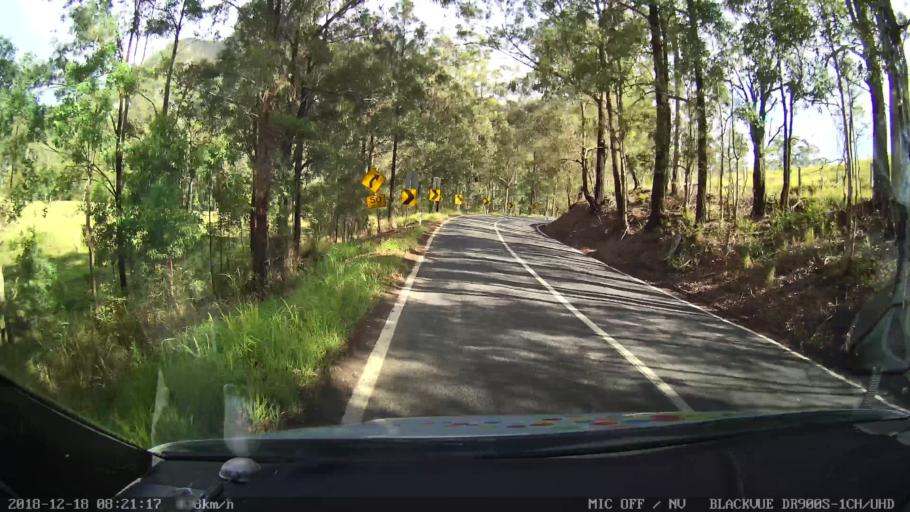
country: AU
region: New South Wales
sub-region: Kyogle
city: Kyogle
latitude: -28.3291
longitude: 152.7193
